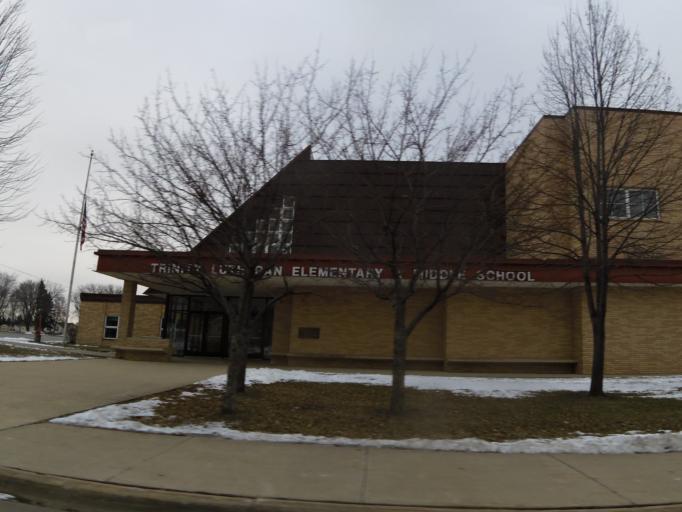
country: US
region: Minnesota
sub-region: Carver County
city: Waconia
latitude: 44.8474
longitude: -93.7785
